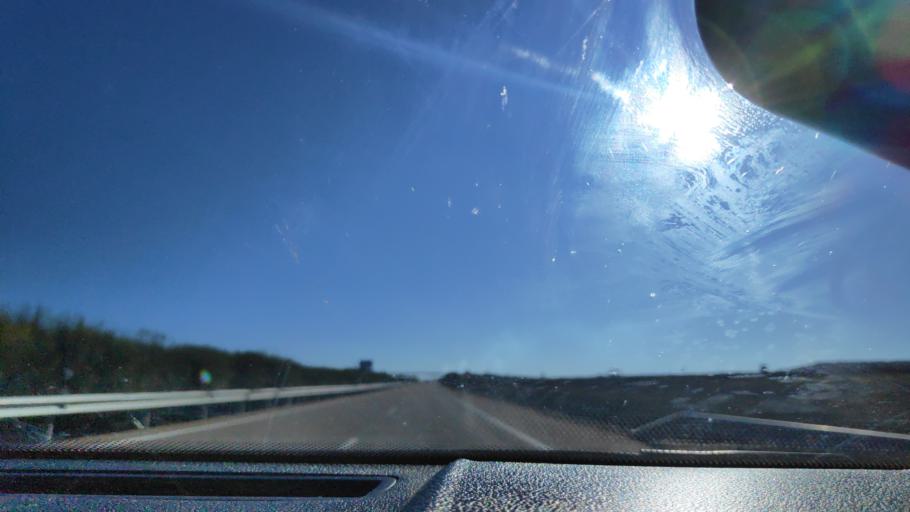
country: ES
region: Extremadura
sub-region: Provincia de Badajoz
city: Villafranca de los Barros
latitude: 38.5187
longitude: -6.3508
